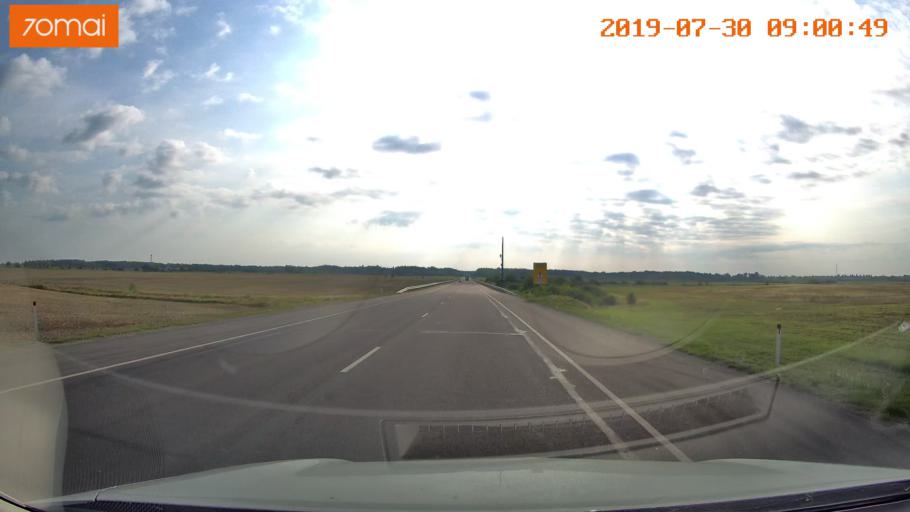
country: RU
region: Kaliningrad
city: Gusev
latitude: 54.6151
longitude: 22.1922
